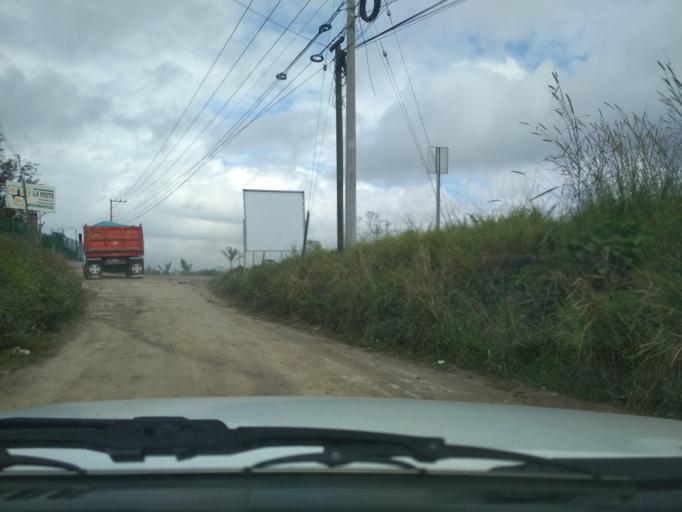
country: MX
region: Veracruz
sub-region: Emiliano Zapata
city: Jacarandas
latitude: 19.5002
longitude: -96.8428
